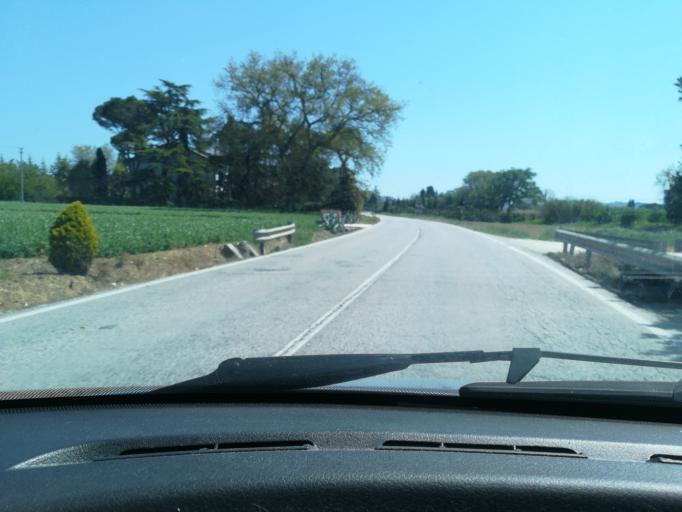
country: IT
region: The Marches
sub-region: Provincia di Ancona
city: Castelfidardo
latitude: 43.4523
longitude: 13.5297
